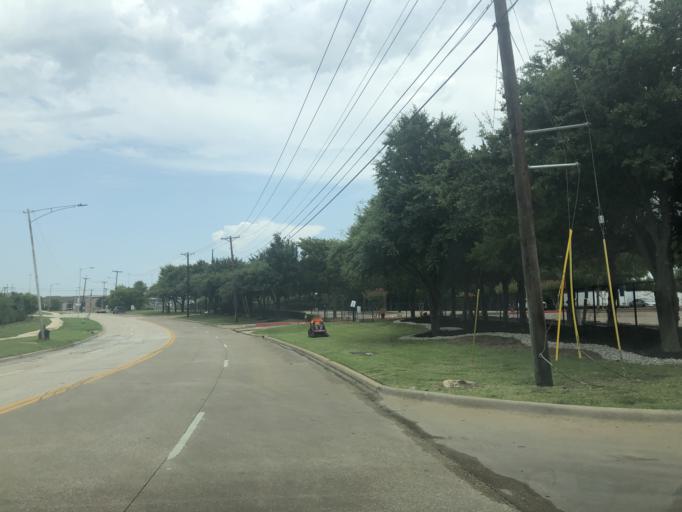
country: US
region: Texas
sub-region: Dallas County
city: Grand Prairie
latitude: 32.7564
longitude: -97.0400
